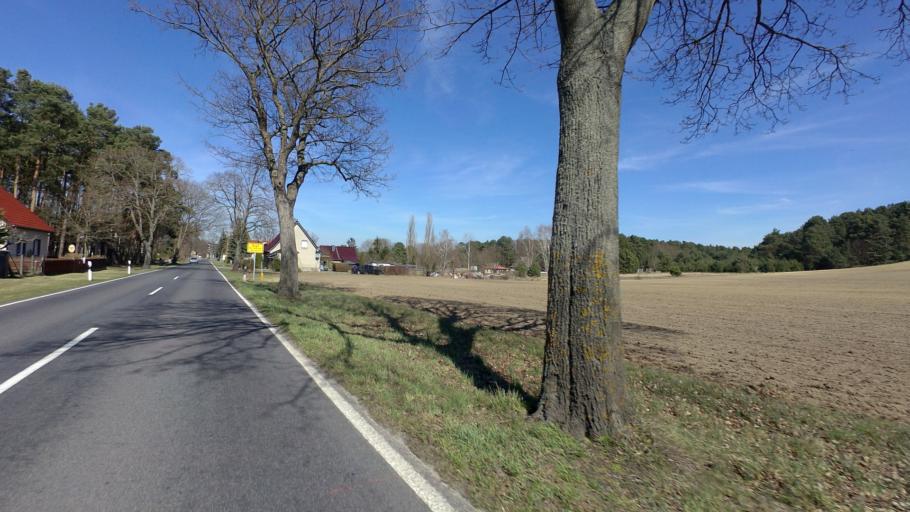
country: DE
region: Brandenburg
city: Storkow
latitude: 52.1900
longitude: 13.9184
